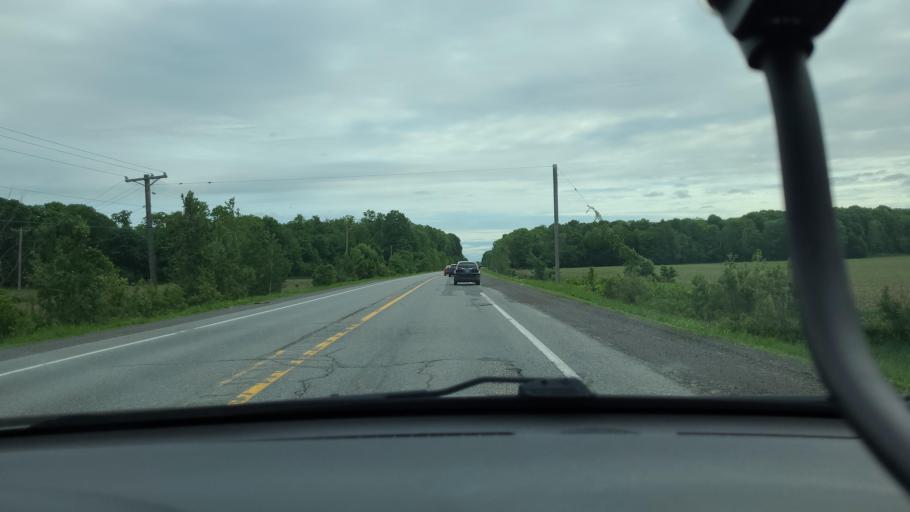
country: CA
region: Quebec
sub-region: Lanaudiere
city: Saint-Jacques
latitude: 45.9407
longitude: -73.5986
